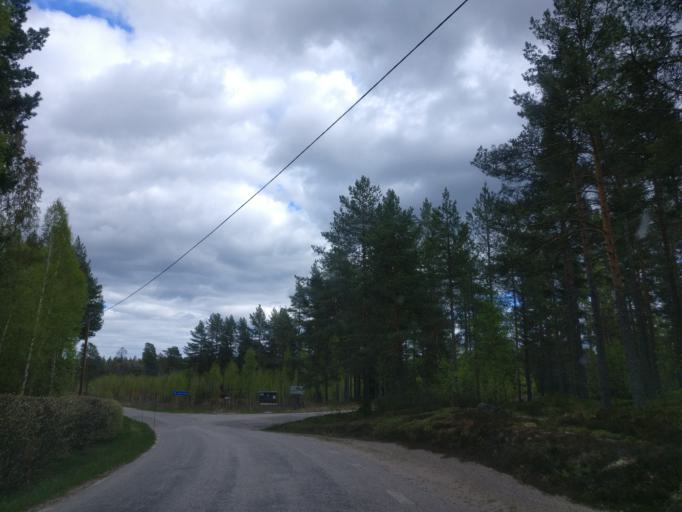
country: SE
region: Gaevleborg
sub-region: Soderhamns Kommun
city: Marielund
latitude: 61.4572
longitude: 17.1038
